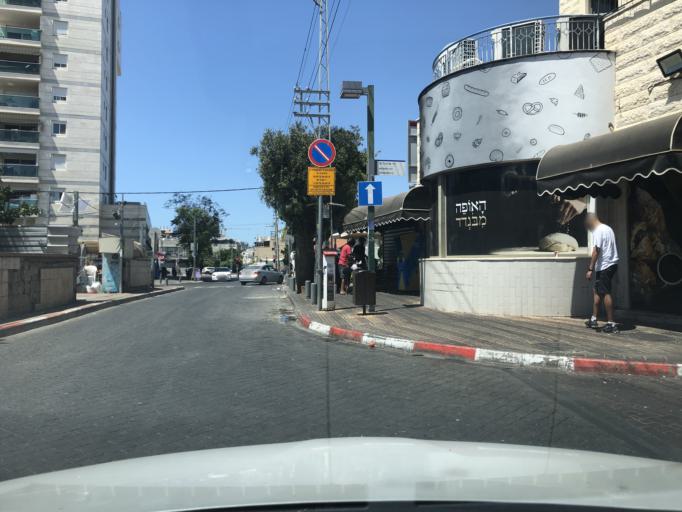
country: IL
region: Tel Aviv
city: Azor
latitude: 32.0462
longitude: 34.7918
